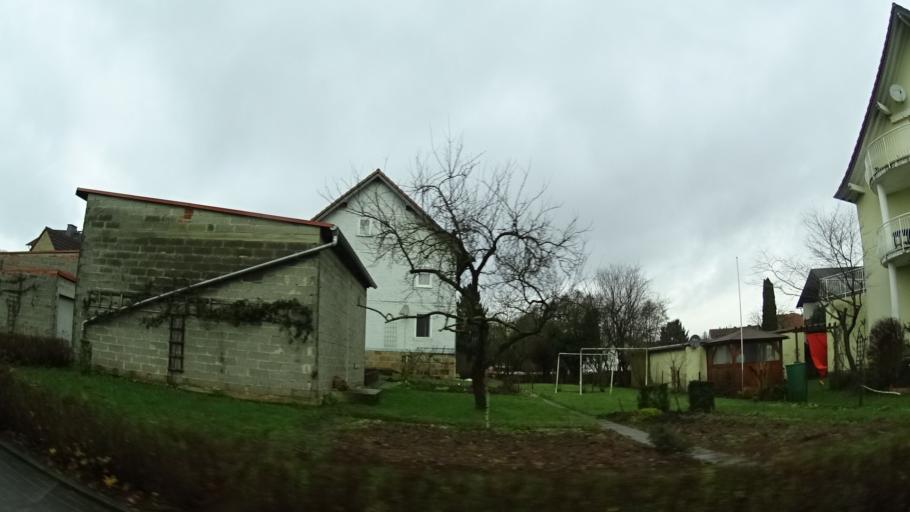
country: DE
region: Hesse
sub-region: Regierungsbezirk Kassel
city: Eichenzell
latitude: 50.4639
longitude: 9.6749
